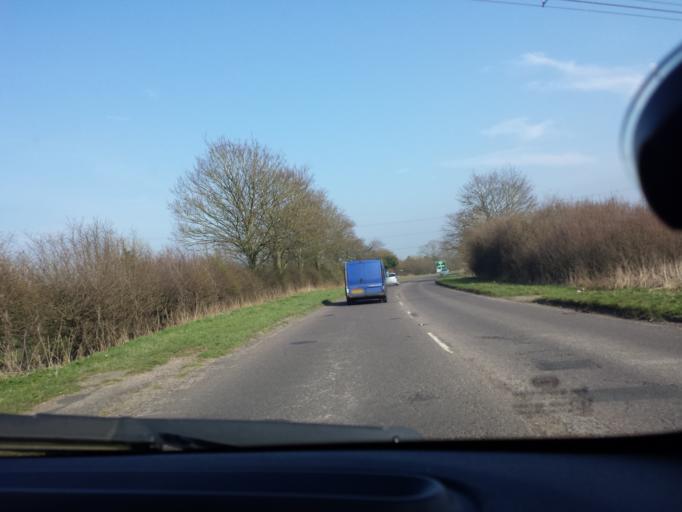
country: GB
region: England
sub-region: Wiltshire
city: Corsham
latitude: 51.4468
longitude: -2.1559
